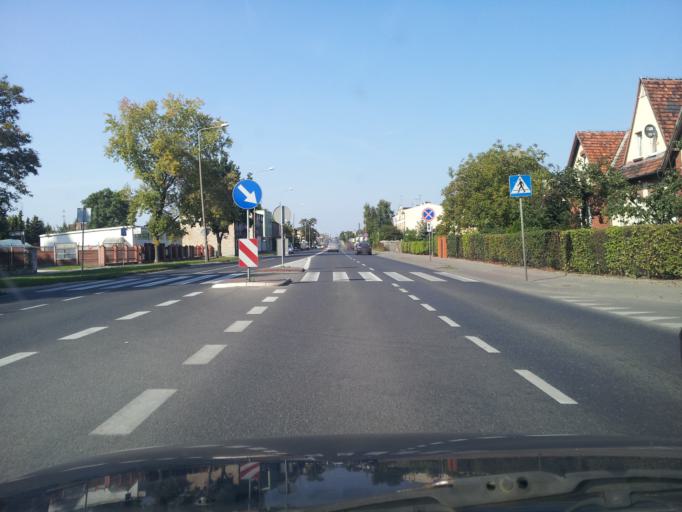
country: PL
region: Kujawsko-Pomorskie
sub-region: Powiat inowroclawski
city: Inowroclaw
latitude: 52.7547
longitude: 18.2563
